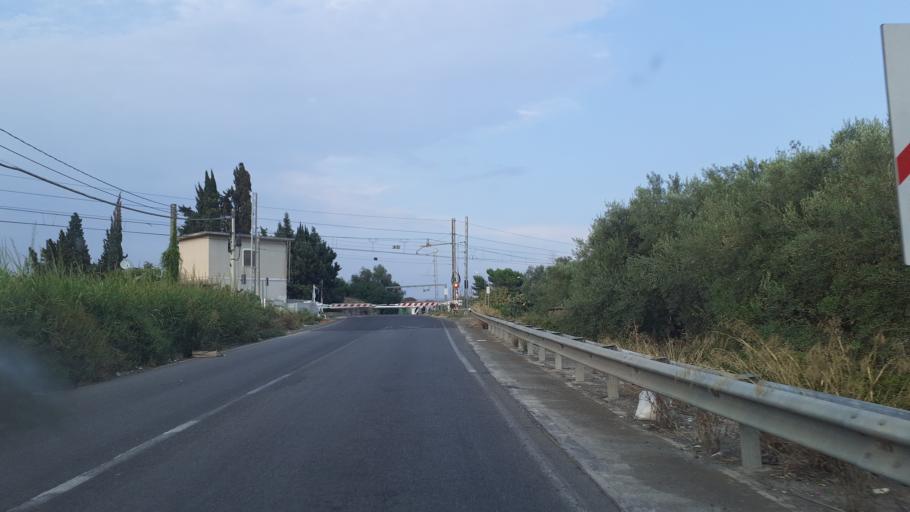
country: IT
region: Sicily
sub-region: Catania
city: Catania
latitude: 37.4554
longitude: 15.0287
